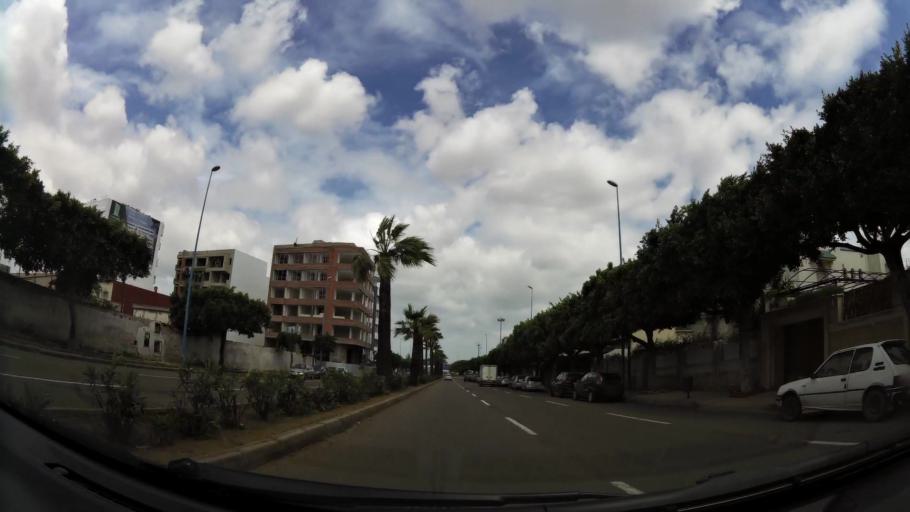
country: MA
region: Grand Casablanca
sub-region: Casablanca
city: Casablanca
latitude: 33.5586
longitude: -7.6253
